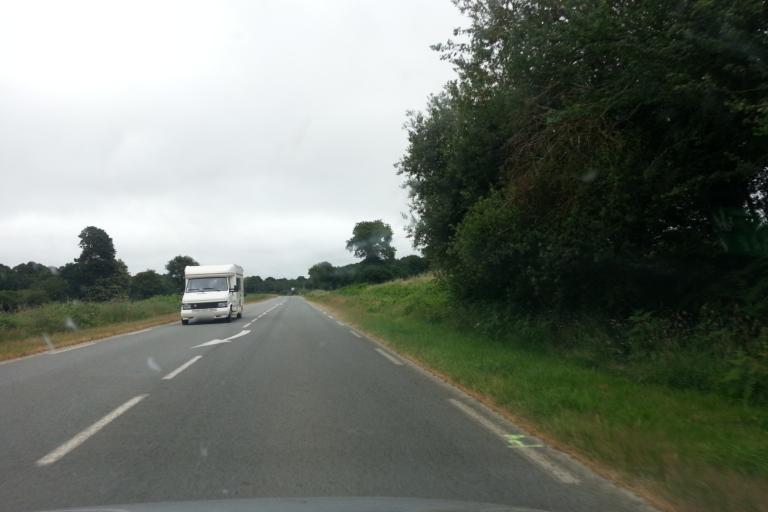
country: FR
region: Brittany
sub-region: Departement des Cotes-d'Armor
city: Gouarec
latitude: 48.2137
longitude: -3.1174
